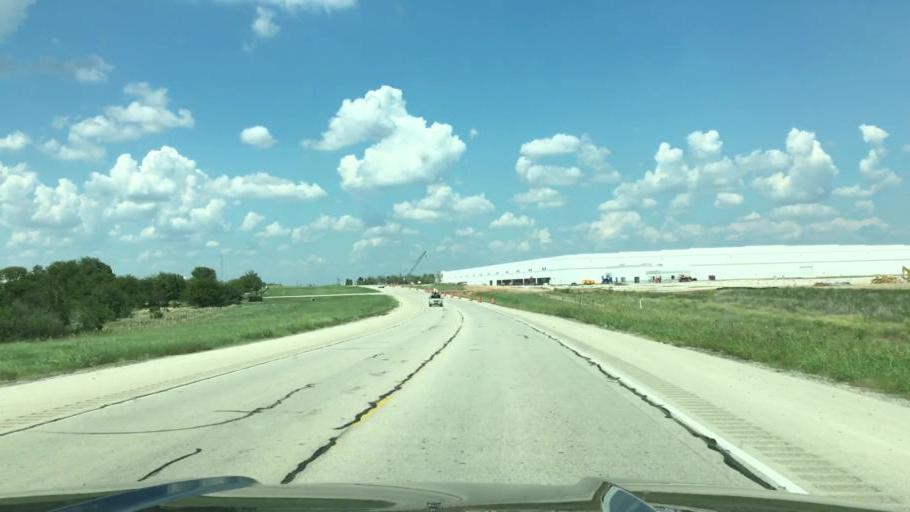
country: US
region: Texas
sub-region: Tarrant County
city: Haslet
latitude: 32.9819
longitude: -97.3421
